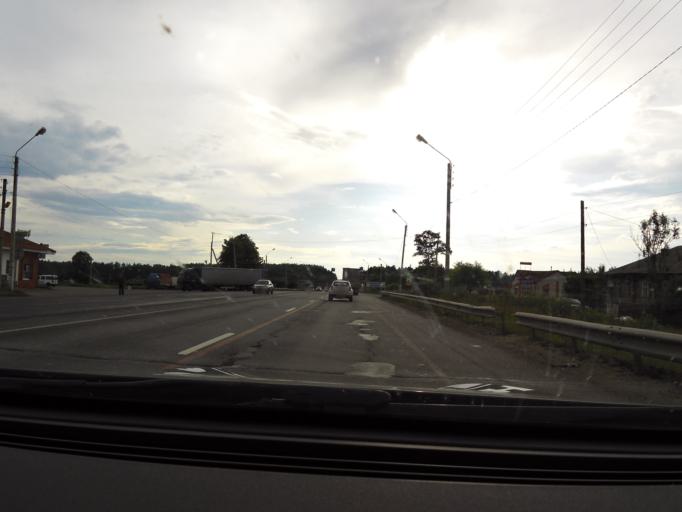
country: RU
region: Vladimir
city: Stepantsevo
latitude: 56.2333
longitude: 41.8007
